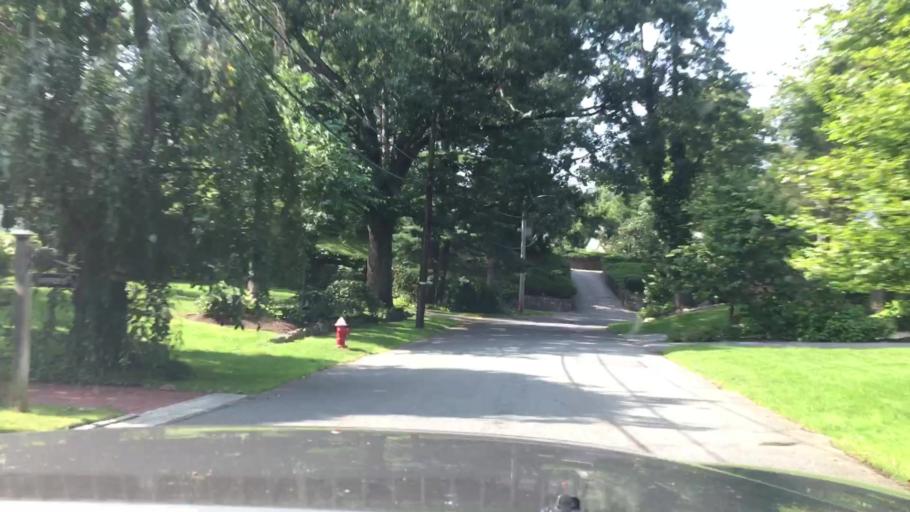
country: US
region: Massachusetts
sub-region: Norfolk County
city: Wellesley
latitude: 42.3130
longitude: -71.2810
